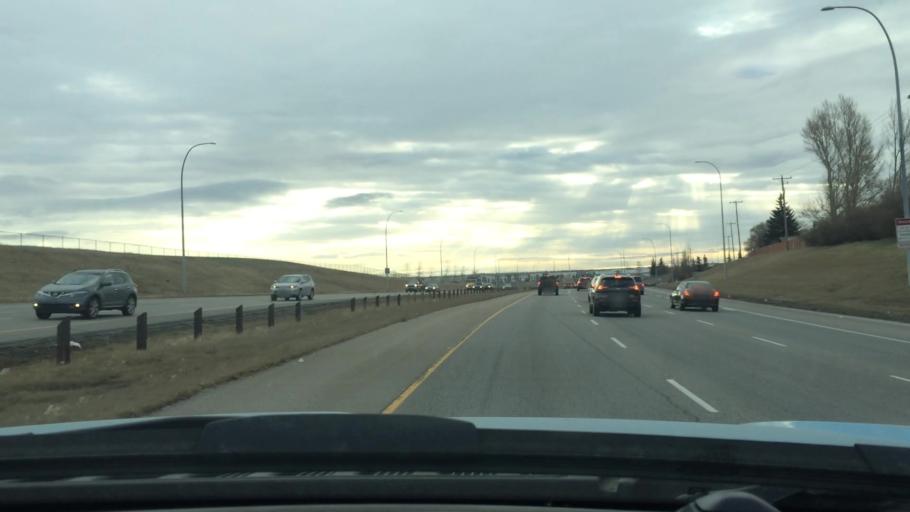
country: CA
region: Alberta
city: Calgary
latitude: 51.1298
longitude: -114.0570
